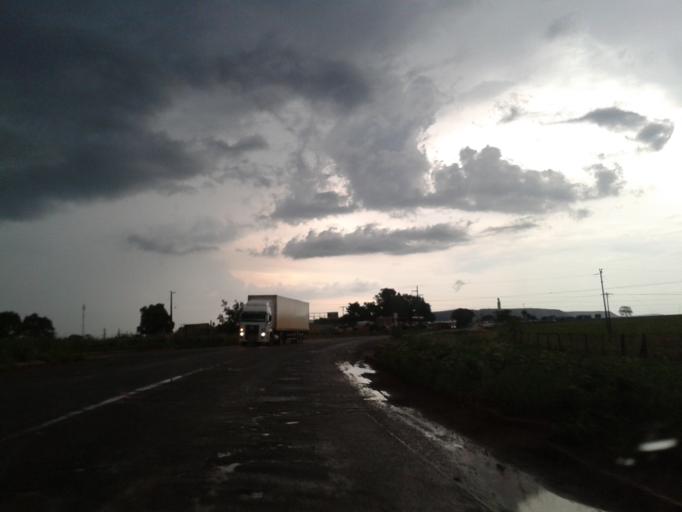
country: BR
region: Goias
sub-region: Quirinopolis
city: Quirinopolis
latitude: -18.4431
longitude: -50.4145
